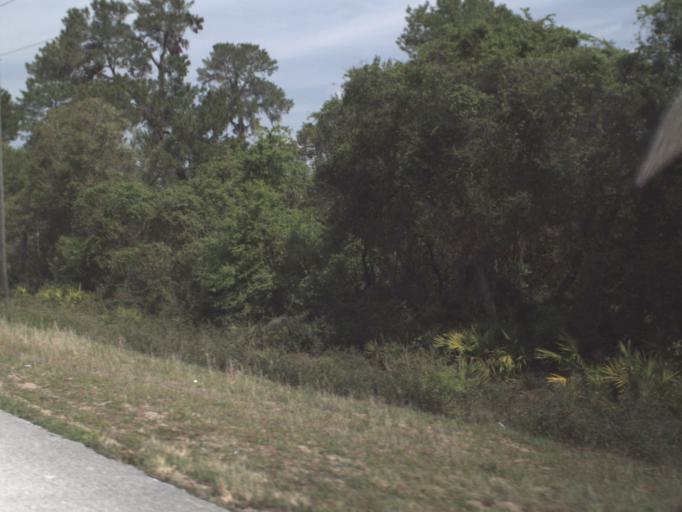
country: US
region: Florida
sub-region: Putnam County
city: Crescent City
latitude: 29.3075
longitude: -81.6836
